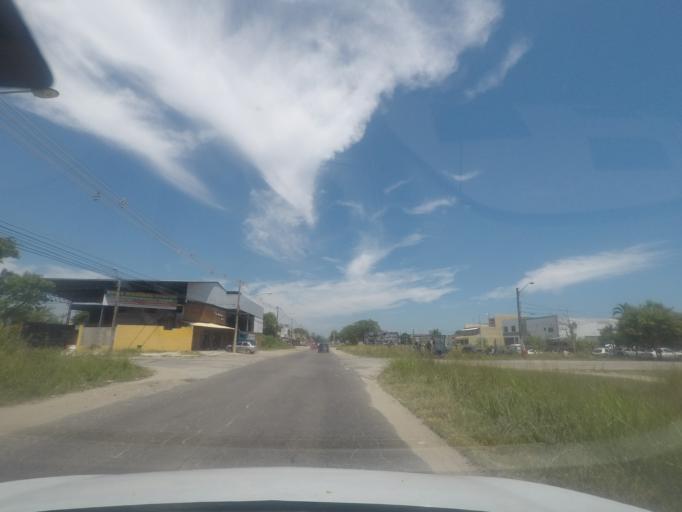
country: BR
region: Rio de Janeiro
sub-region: Itaguai
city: Itaguai
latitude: -22.9787
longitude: -43.6696
